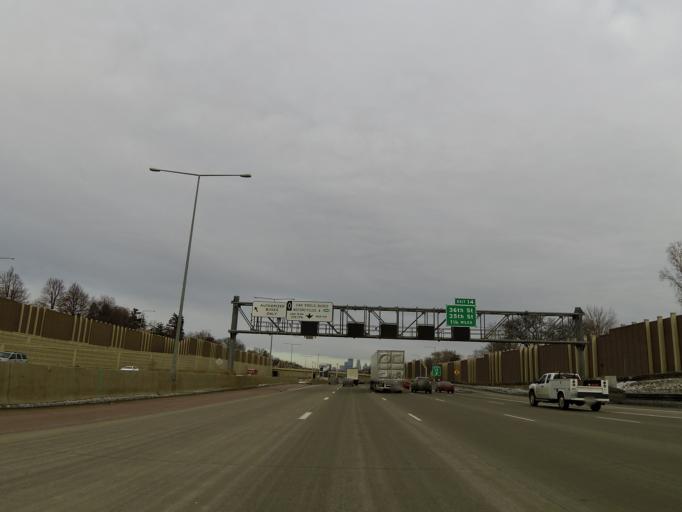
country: US
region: Minnesota
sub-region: Hennepin County
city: Richfield
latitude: 44.9163
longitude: -93.2747
